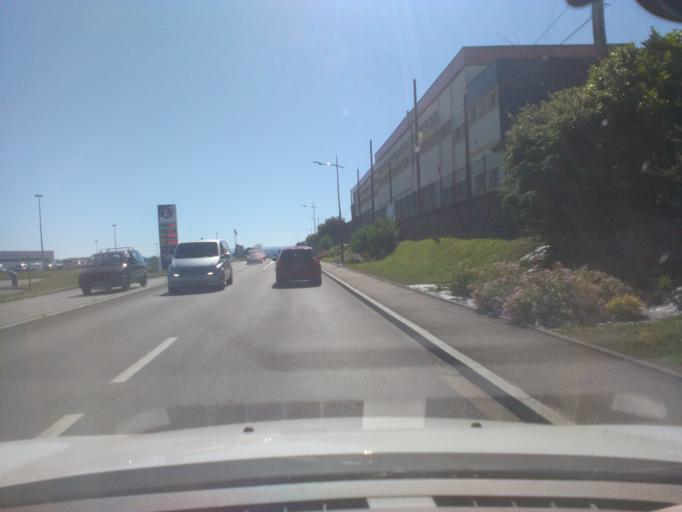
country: FR
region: Lorraine
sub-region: Departement des Vosges
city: Golbey
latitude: 48.1908
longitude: 6.4188
